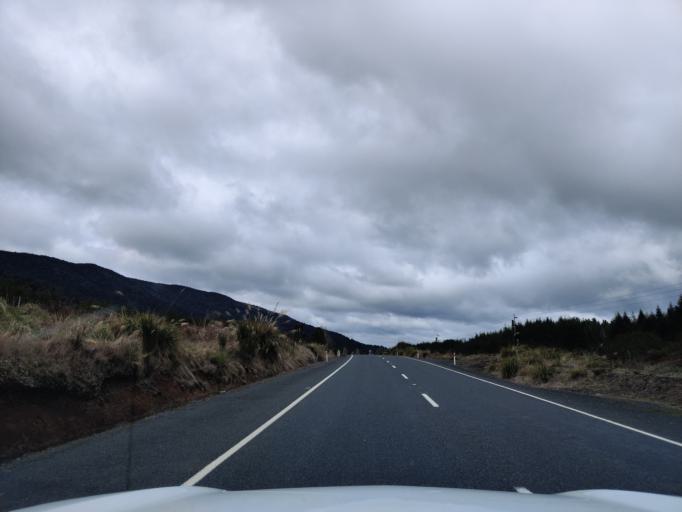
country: NZ
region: Manawatu-Wanganui
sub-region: Ruapehu District
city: Waiouru
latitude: -39.2063
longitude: 175.4026
